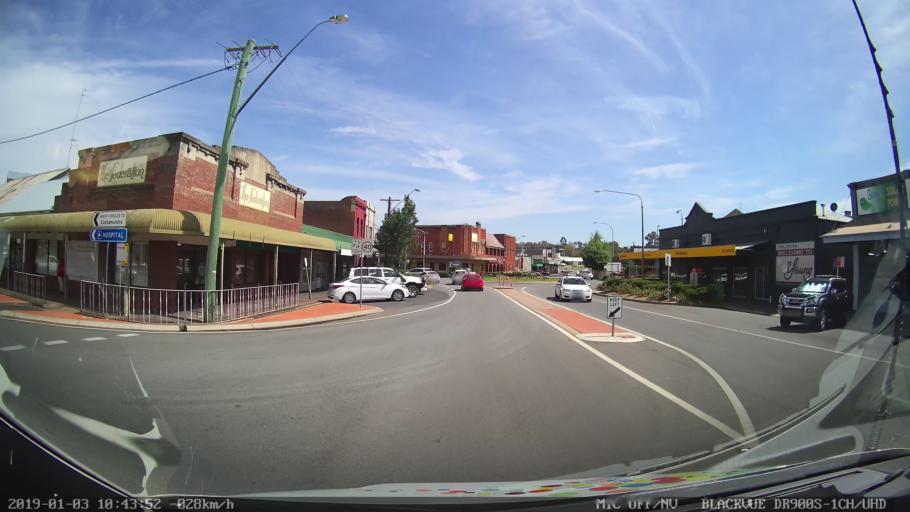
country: AU
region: New South Wales
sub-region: Young
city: Young
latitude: -34.3135
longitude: 148.2955
